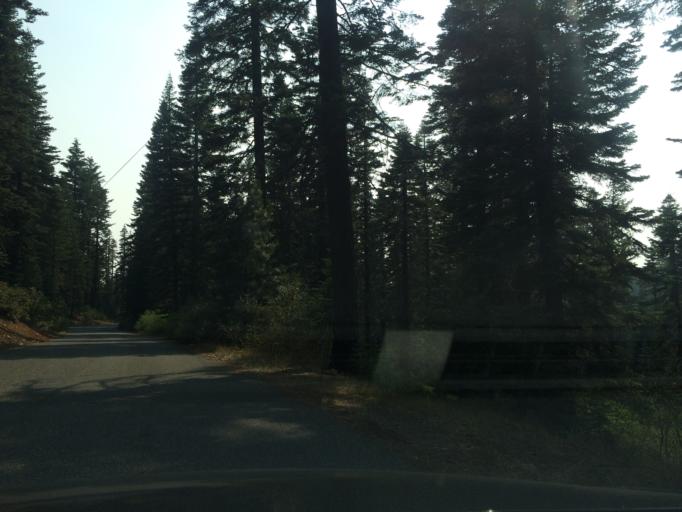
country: US
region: California
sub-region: Sierra County
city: Downieville
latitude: 39.3839
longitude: -120.6743
